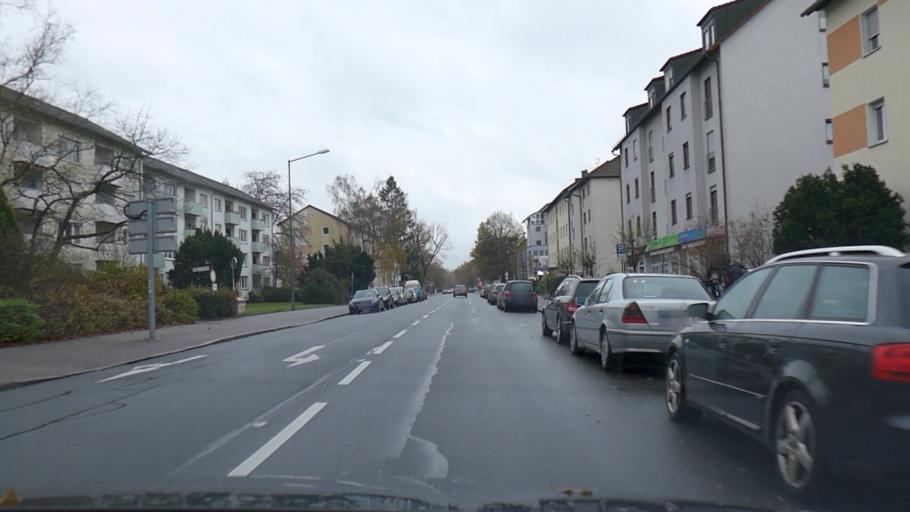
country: DE
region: Bavaria
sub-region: Regierungsbezirk Mittelfranken
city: Erlangen
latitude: 49.5908
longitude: 11.0172
